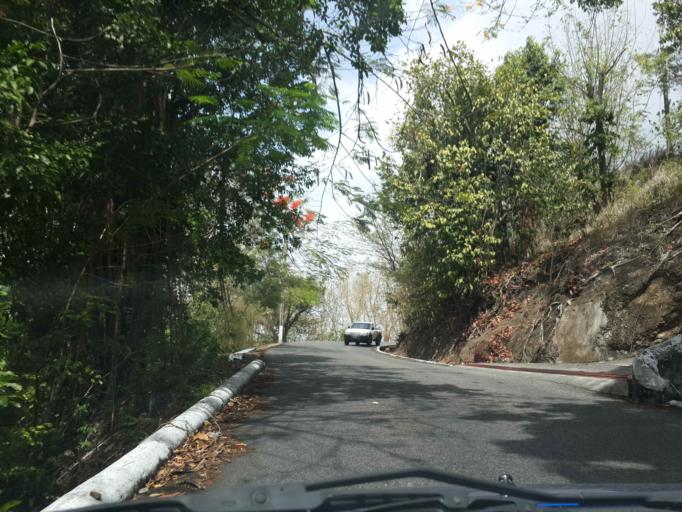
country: LC
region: Castries Quarter
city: Castries
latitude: 14.0068
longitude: -60.9980
